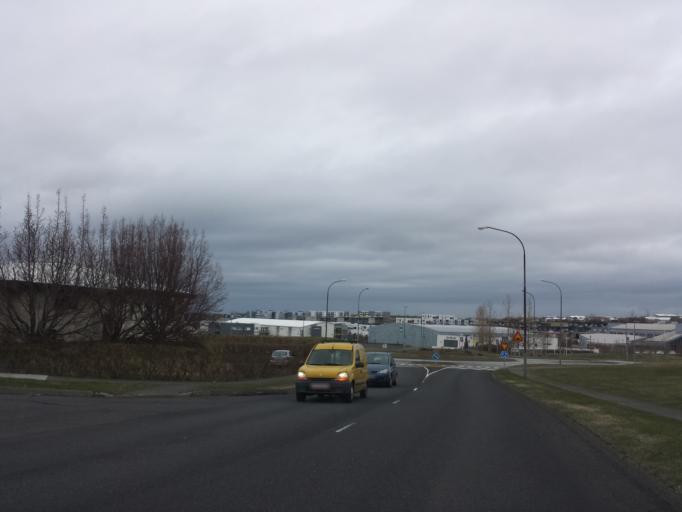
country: IS
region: Capital Region
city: Gardabaer
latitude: 64.0916
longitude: -21.9035
